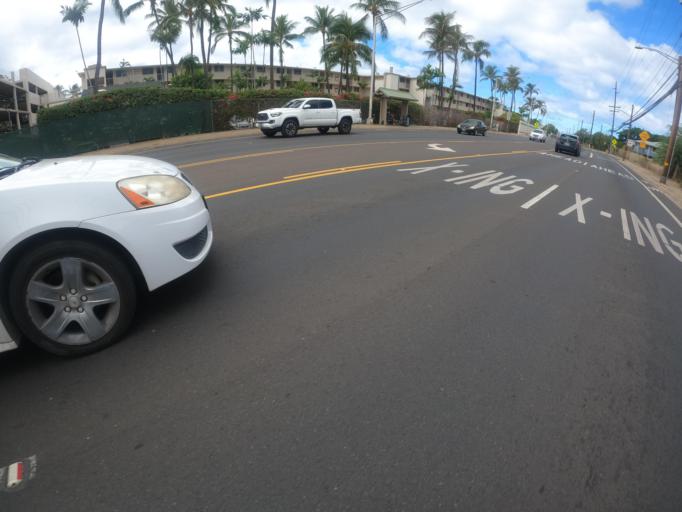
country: US
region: Hawaii
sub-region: Honolulu County
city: Makaha
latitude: 21.4584
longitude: -158.2027
